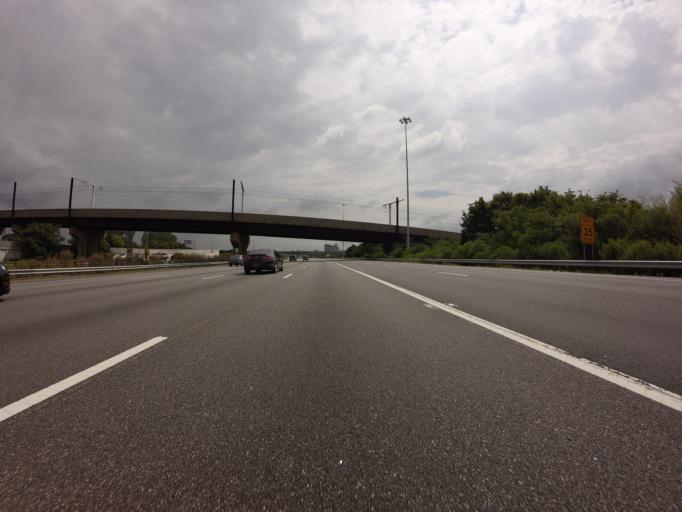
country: US
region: Pennsylvania
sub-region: Delaware County
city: Folcroft
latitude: 39.8763
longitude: -75.2570
